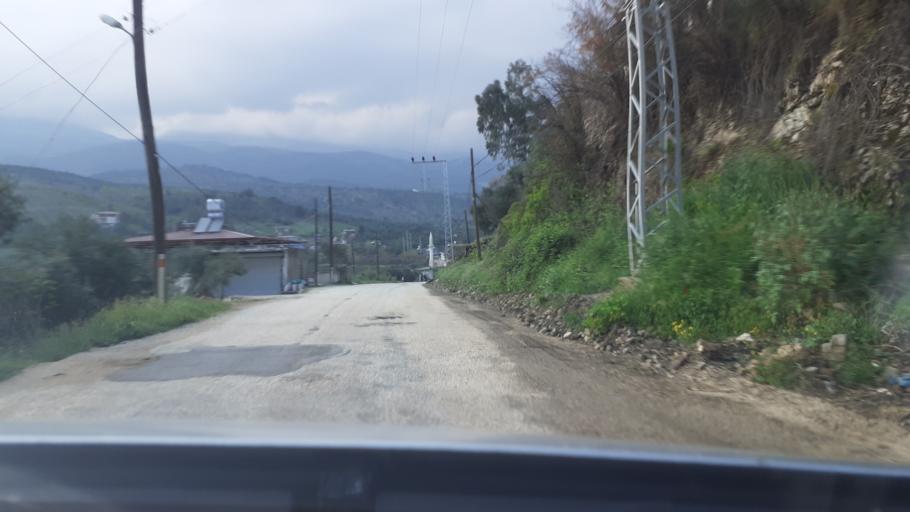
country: TR
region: Hatay
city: Kirikhan
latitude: 36.5027
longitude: 36.3251
